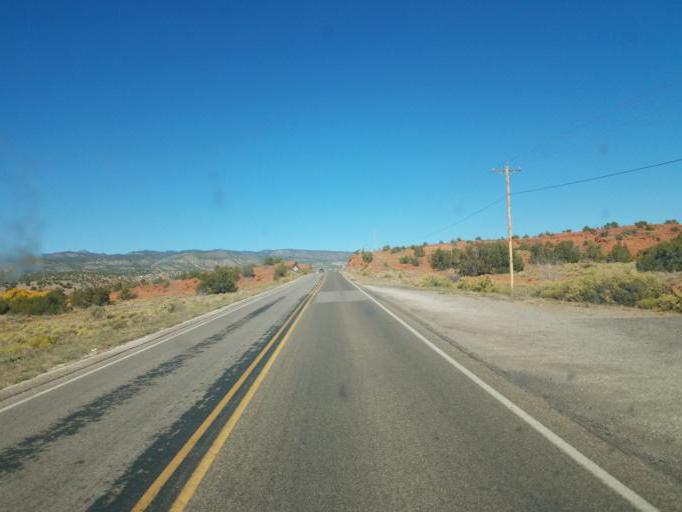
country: US
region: New Mexico
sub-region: Sandoval County
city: Jemez Pueblo
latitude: 35.6461
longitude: -106.7265
